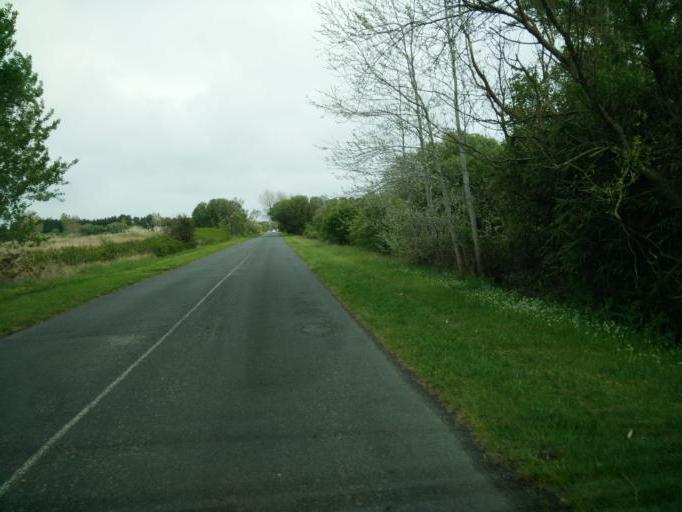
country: FR
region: Brittany
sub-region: Departement du Finistere
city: Plobannalec-Lesconil
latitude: 47.8037
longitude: -4.2033
